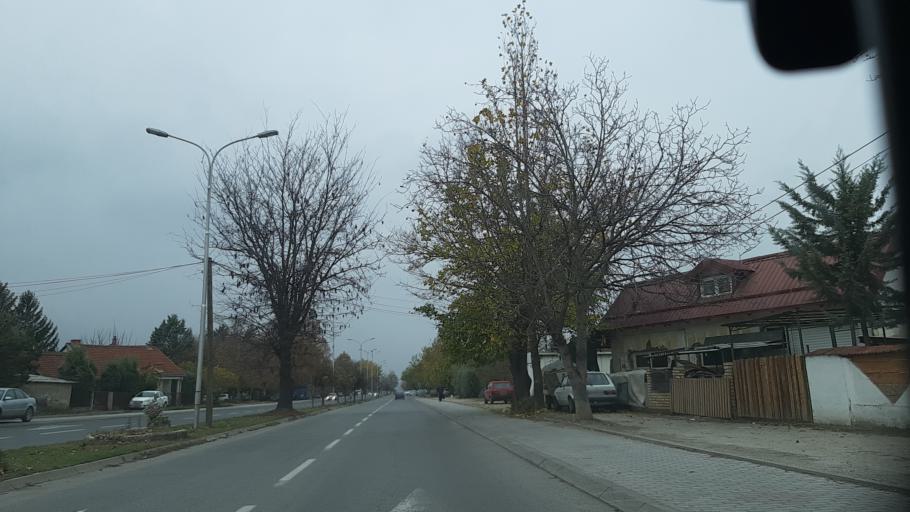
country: MK
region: Kisela Voda
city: Usje
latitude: 41.9730
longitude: 21.4741
